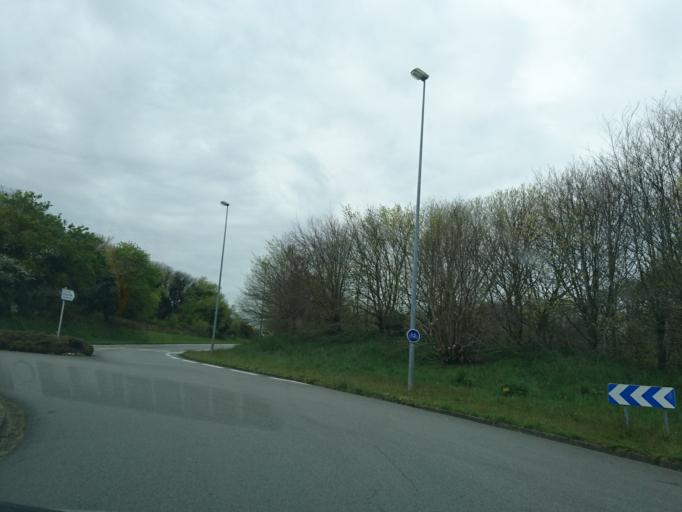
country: FR
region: Brittany
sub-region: Departement du Finistere
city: Roscanvel
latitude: 48.3626
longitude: -4.5636
